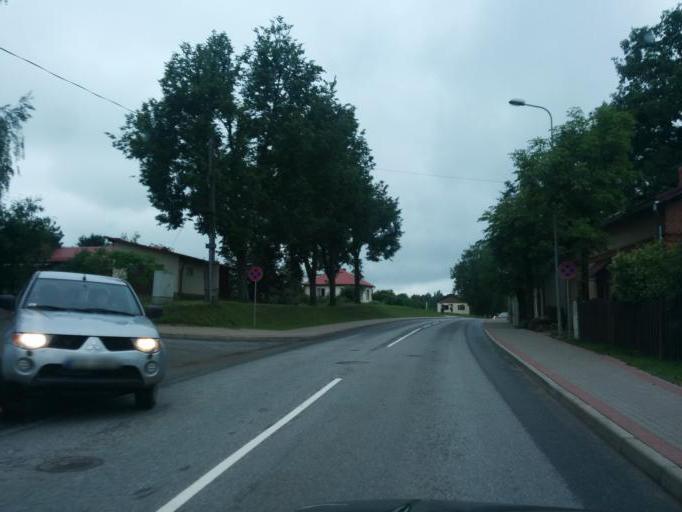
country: LV
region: Smiltene
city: Smiltene
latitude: 57.4279
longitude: 25.8931
